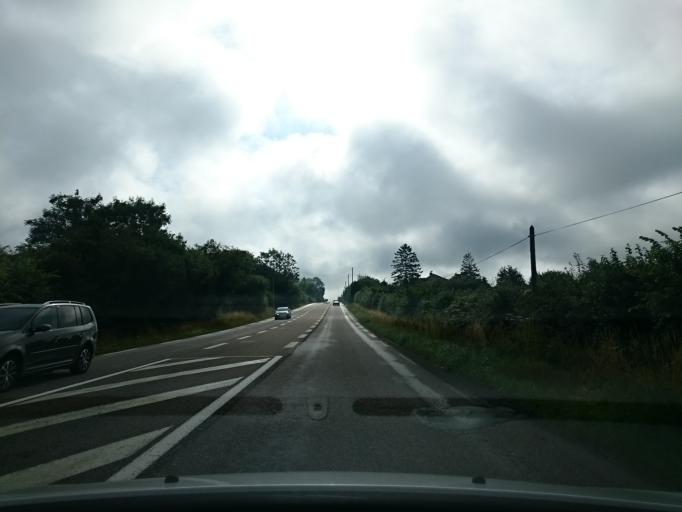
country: FR
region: Lower Normandy
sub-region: Departement du Calvados
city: Saint-Desir
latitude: 49.1353
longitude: 0.1390
